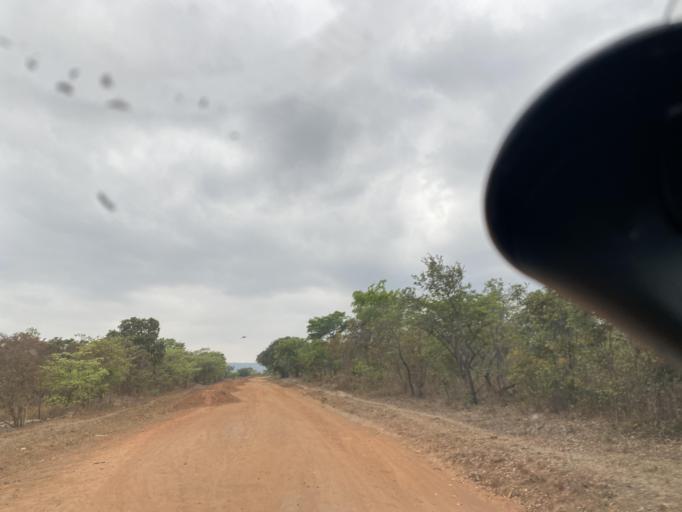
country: ZM
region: Lusaka
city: Chongwe
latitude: -15.2173
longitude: 28.7537
